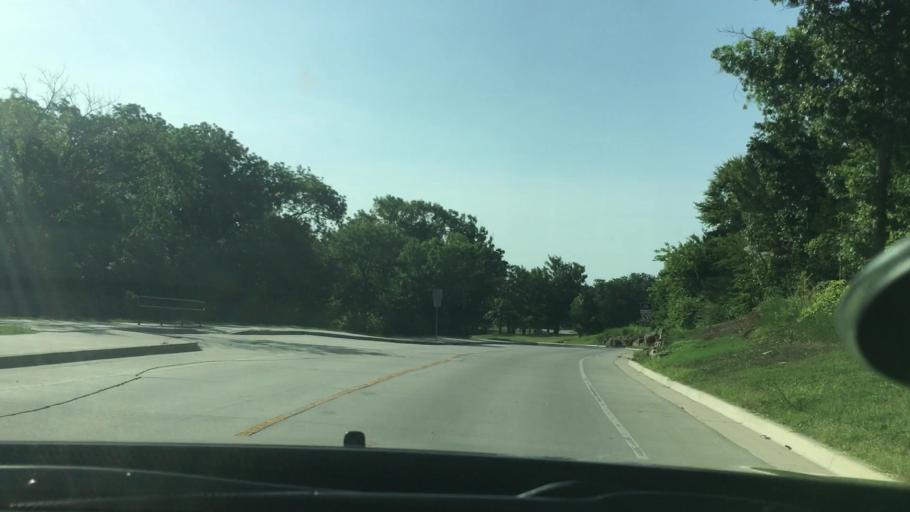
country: US
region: Oklahoma
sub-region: Pontotoc County
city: Ada
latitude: 34.7685
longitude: -96.6597
